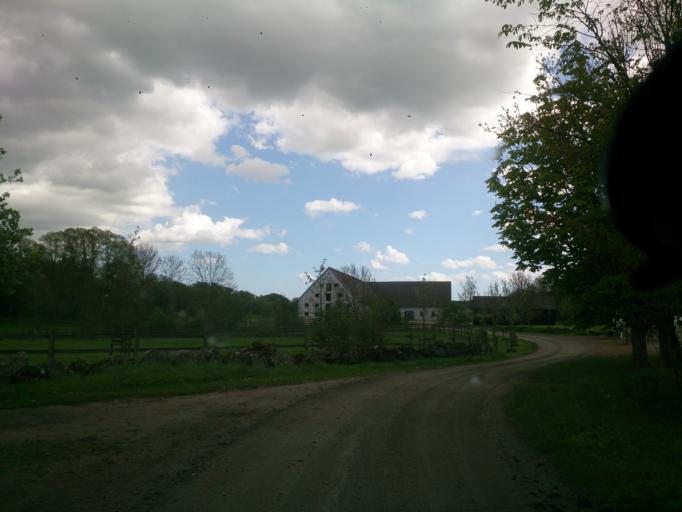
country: SE
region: Skane
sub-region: Sjobo Kommun
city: Sjoebo
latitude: 55.5597
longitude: 13.7089
